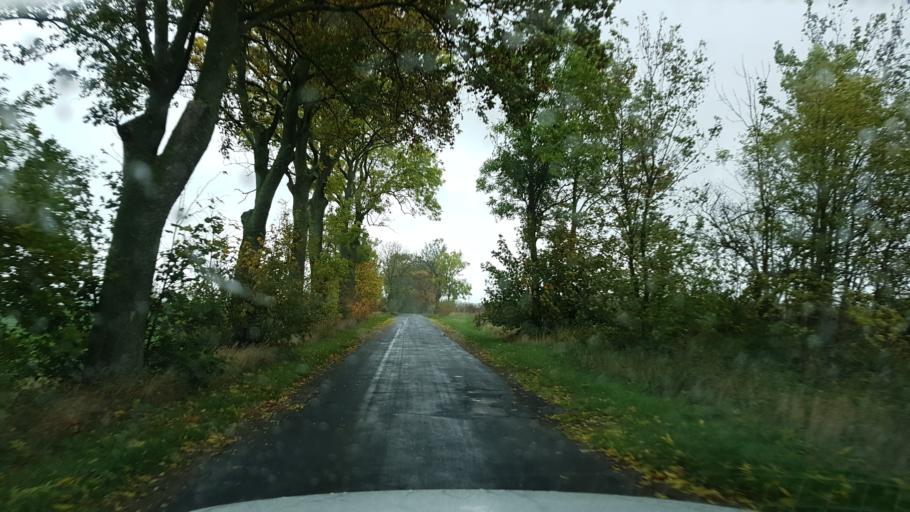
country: PL
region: West Pomeranian Voivodeship
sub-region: Powiat pyrzycki
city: Kozielice
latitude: 53.0358
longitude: 14.8534
